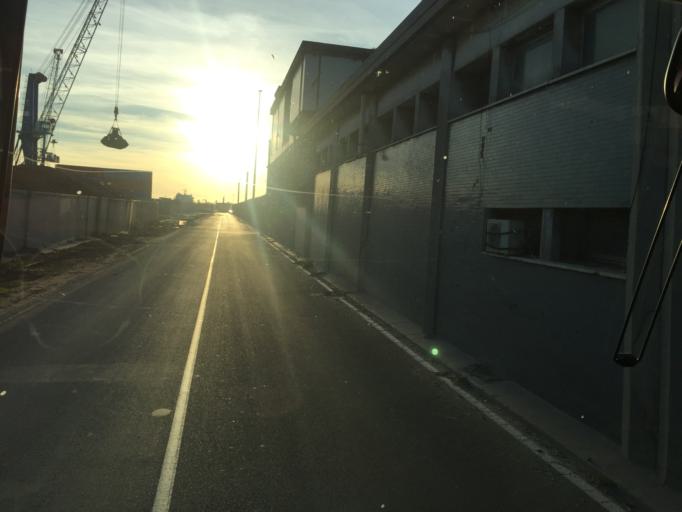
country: IT
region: Tuscany
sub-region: Provincia di Livorno
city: Livorno
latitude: 43.5535
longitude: 10.2980
